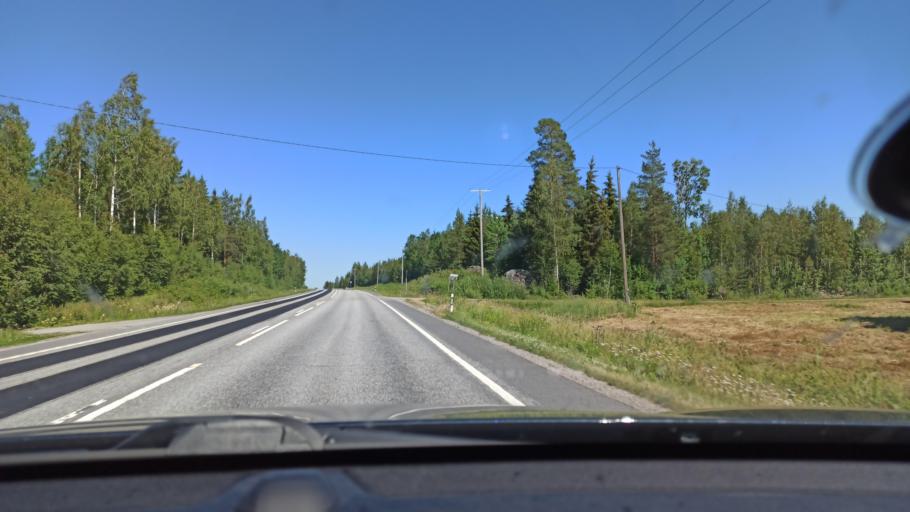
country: FI
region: Ostrobothnia
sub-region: Vaasa
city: Voera
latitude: 63.2153
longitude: 22.2044
